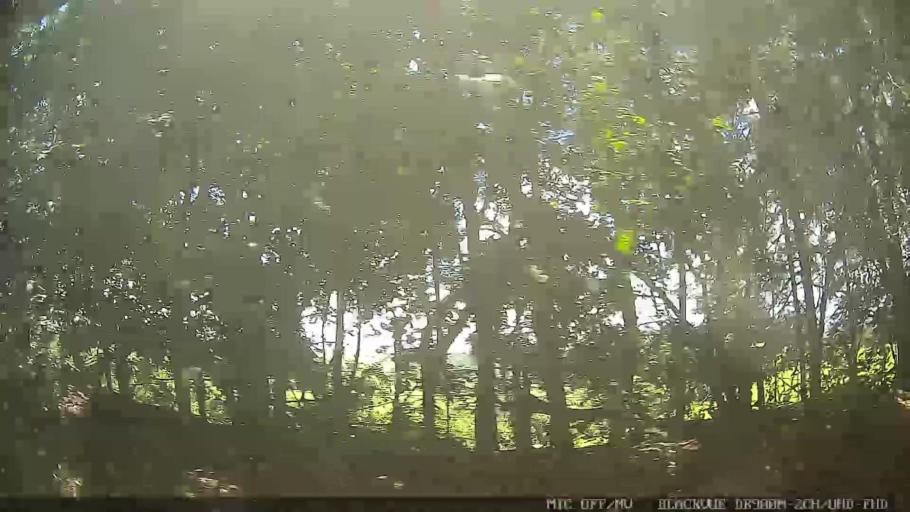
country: BR
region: Sao Paulo
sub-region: Braganca Paulista
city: Braganca Paulista
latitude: -23.0267
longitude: -46.4712
